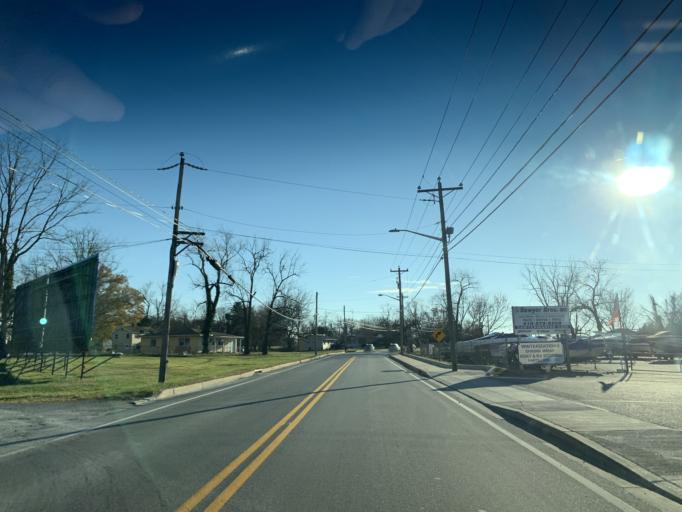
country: US
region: Delaware
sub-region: New Castle County
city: Middletown
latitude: 39.4025
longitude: -75.8682
